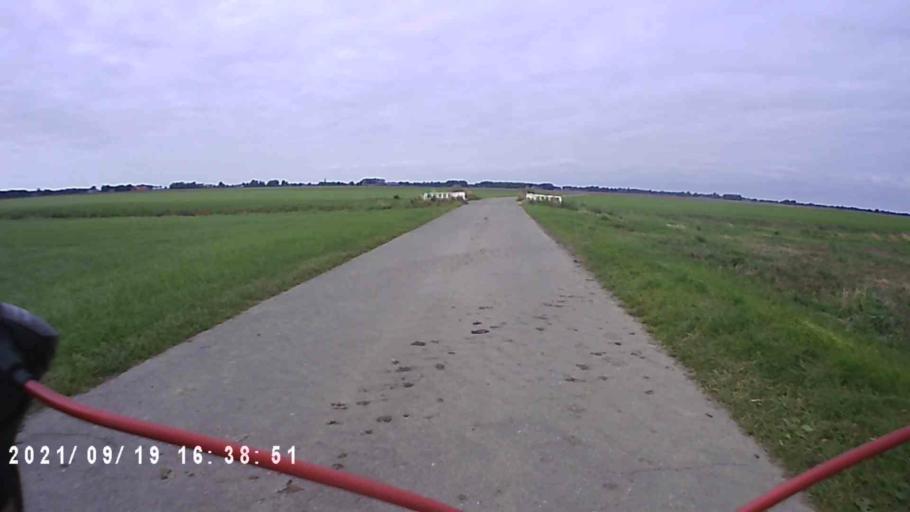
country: NL
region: Groningen
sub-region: Gemeente  Oldambt
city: Winschoten
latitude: 53.1892
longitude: 7.1316
